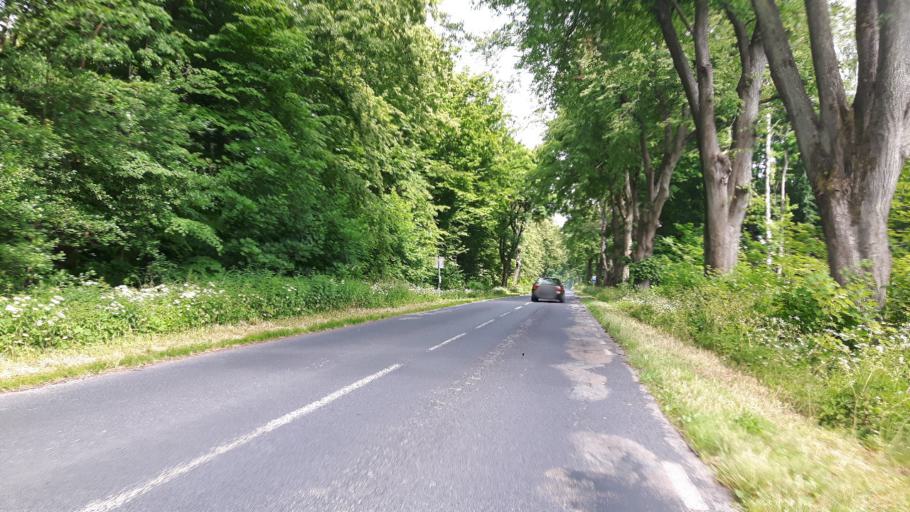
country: PL
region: Warmian-Masurian Voivodeship
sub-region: Powiat braniewski
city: Frombork
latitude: 54.3621
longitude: 19.7408
